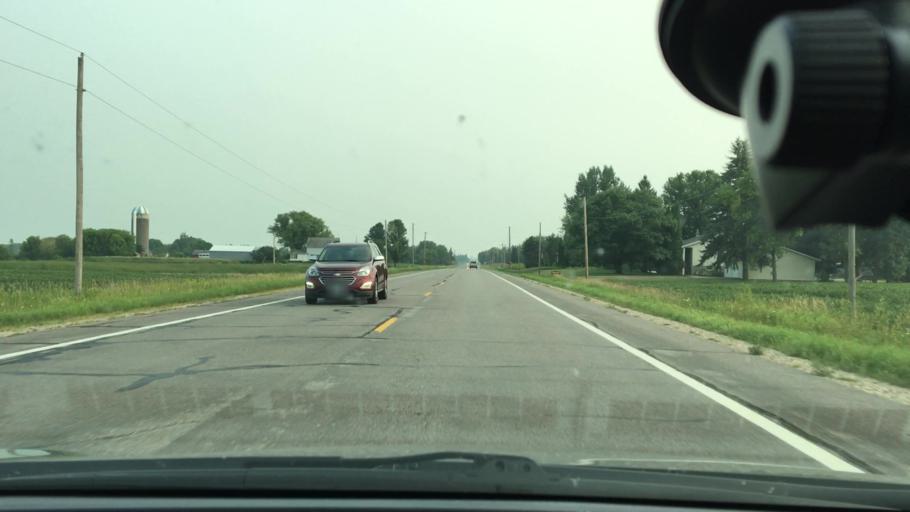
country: US
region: Minnesota
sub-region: Wright County
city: Albertville
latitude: 45.2726
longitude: -93.6636
